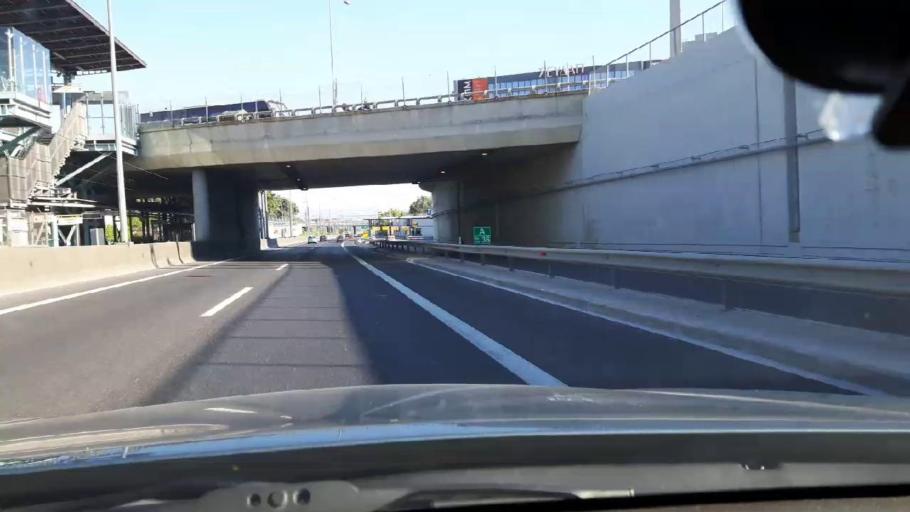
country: GR
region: Attica
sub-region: Nomarchia Anatolikis Attikis
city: Pallini
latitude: 37.9946
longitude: 23.8725
